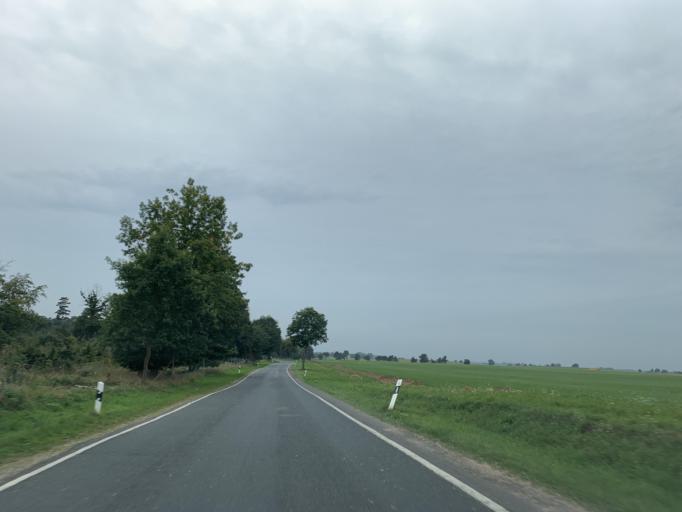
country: DE
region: Mecklenburg-Vorpommern
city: Woldegk
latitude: 53.3368
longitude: 13.6059
